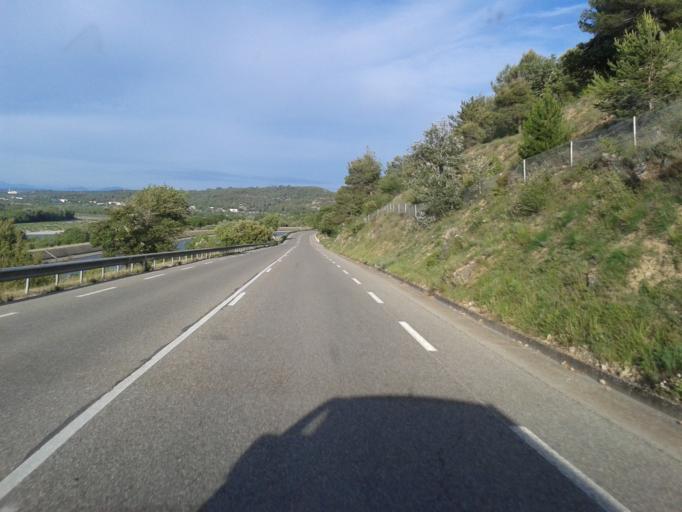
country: FR
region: Provence-Alpes-Cote d'Azur
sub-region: Departement du Vaucluse
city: Beaumont-de-Pertuis
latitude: 43.6888
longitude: 5.6949
